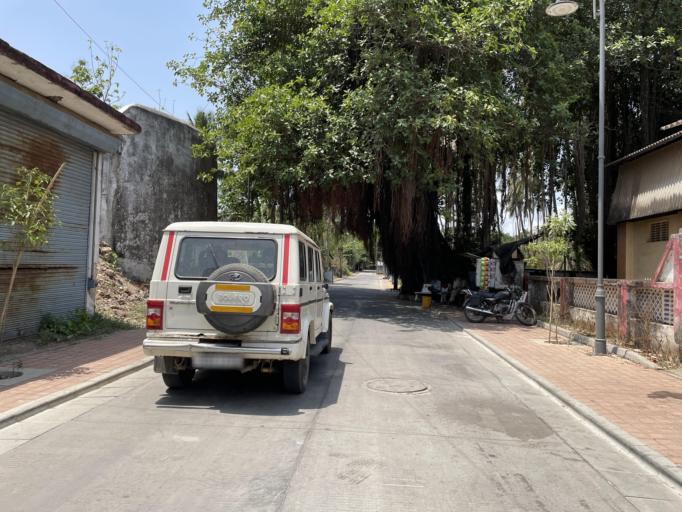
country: IN
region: Daman and Diu
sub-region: Daman District
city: Daman
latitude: 20.4075
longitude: 72.8329
